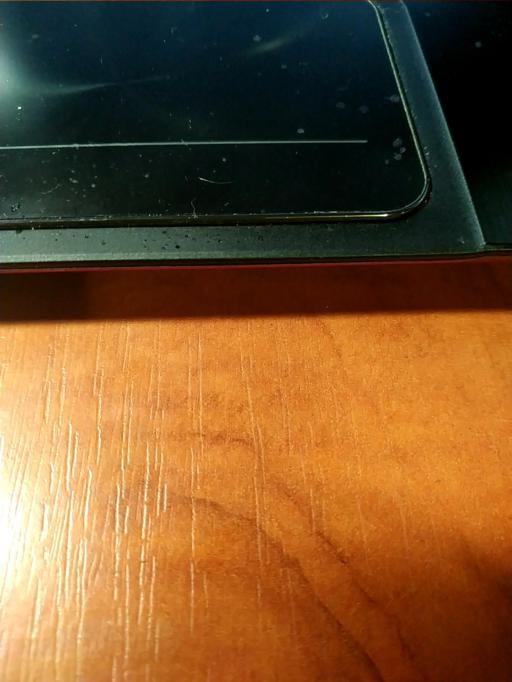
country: RU
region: Tverskaya
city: Likhoslavl'
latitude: 57.2209
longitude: 35.5898
